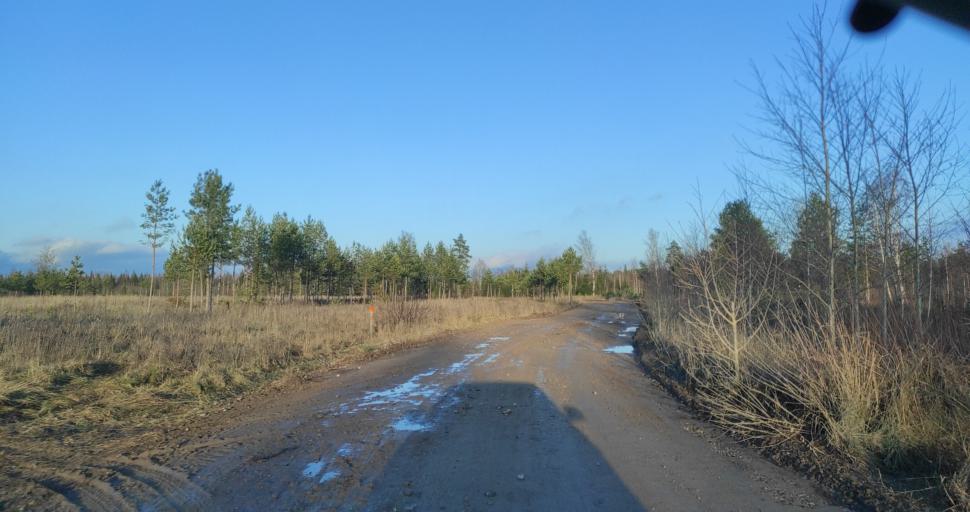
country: LV
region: Kuldigas Rajons
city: Kuldiga
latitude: 57.0518
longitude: 21.8662
